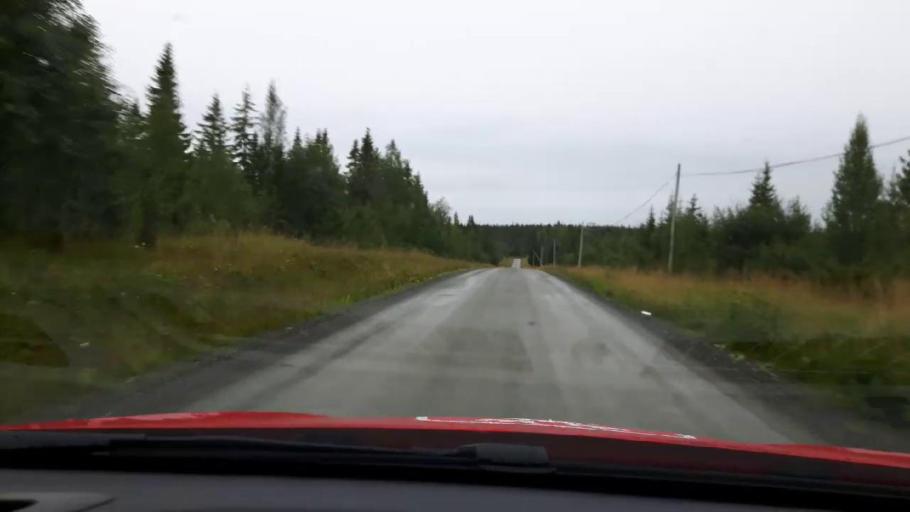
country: SE
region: Jaemtland
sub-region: Are Kommun
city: Are
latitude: 63.4395
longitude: 12.8076
